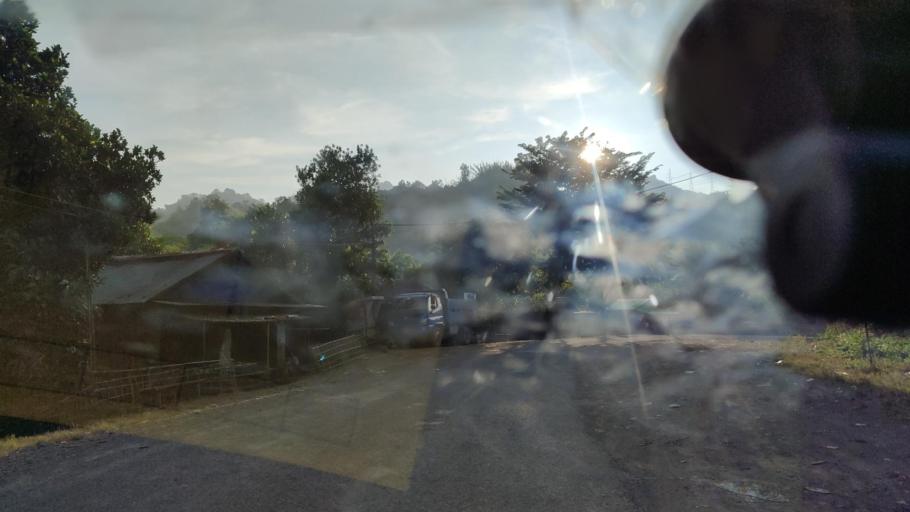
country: MM
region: Magway
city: Minbu
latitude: 19.8608
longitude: 94.1399
